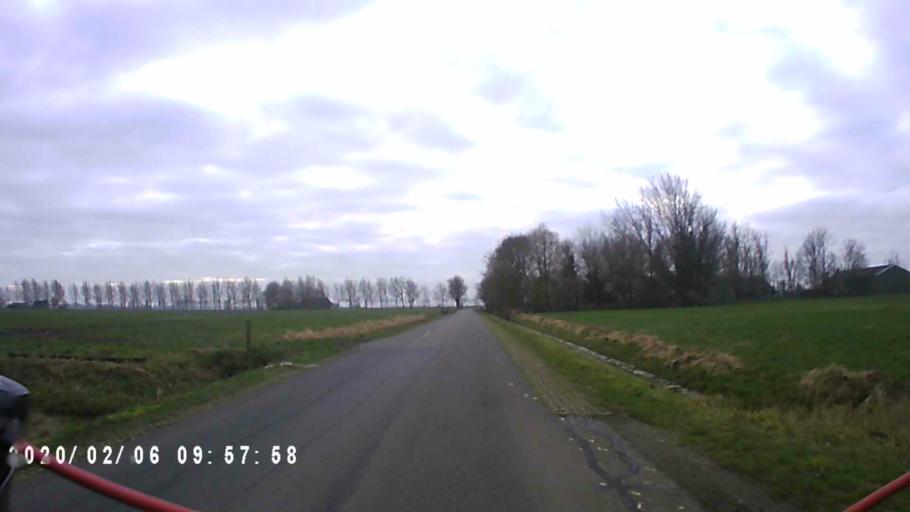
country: NL
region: Groningen
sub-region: Gemeente Zuidhorn
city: Aduard
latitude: 53.2728
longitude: 6.4964
